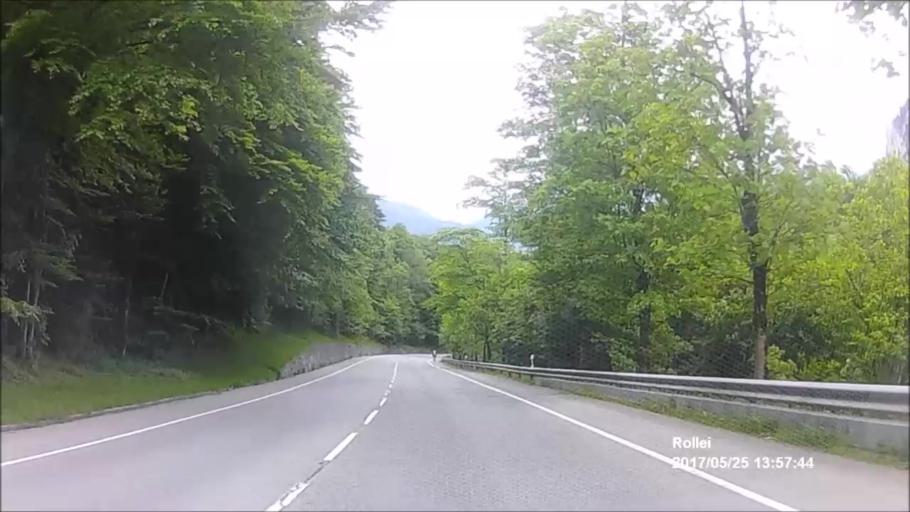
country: DE
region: Bavaria
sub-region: Upper Bavaria
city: Marktschellenberg
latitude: 47.6642
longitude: 13.0353
